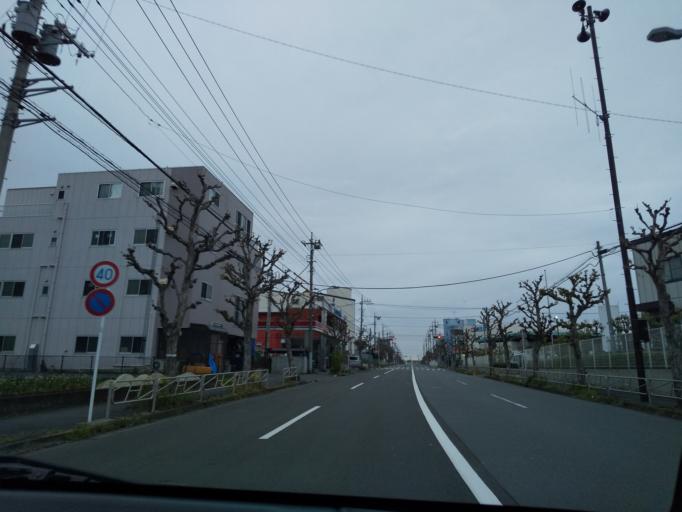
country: JP
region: Tokyo
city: Hino
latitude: 35.6767
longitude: 139.3719
